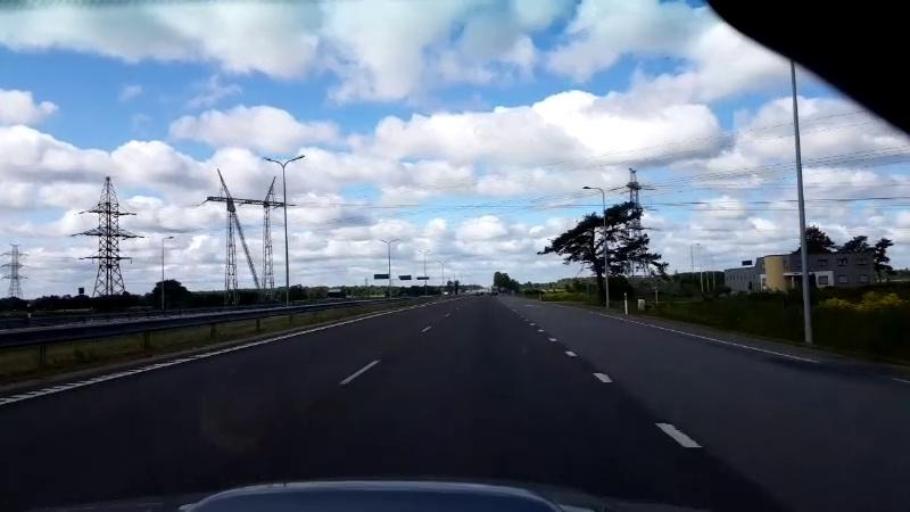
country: EE
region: Harju
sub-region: Saue vald
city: Laagri
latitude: 59.3342
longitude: 24.6053
